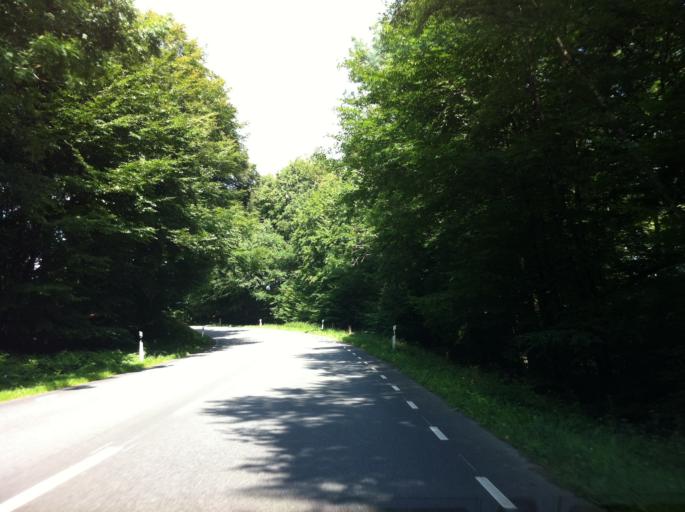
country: SE
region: Skane
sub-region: Klippans Kommun
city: Ljungbyhed
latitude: 55.9906
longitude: 13.2803
